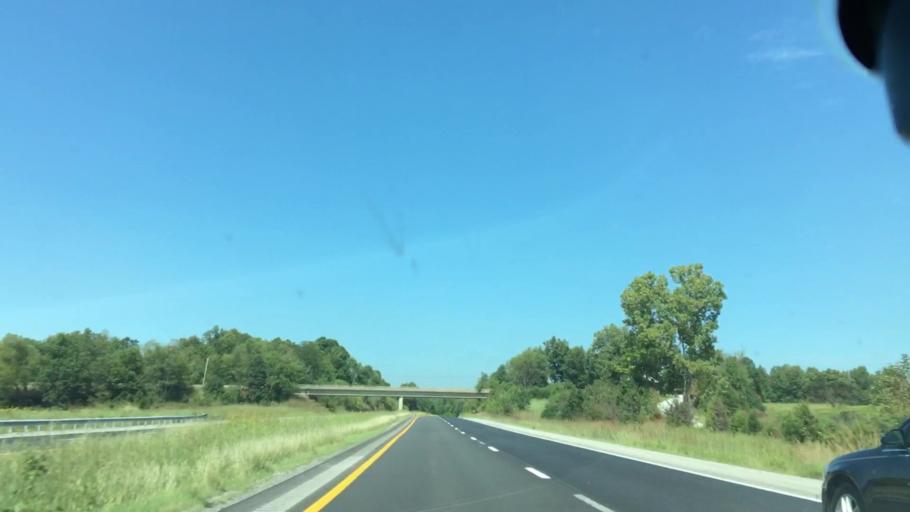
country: US
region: Kentucky
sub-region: Hopkins County
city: Madisonville
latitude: 37.4572
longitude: -87.4793
